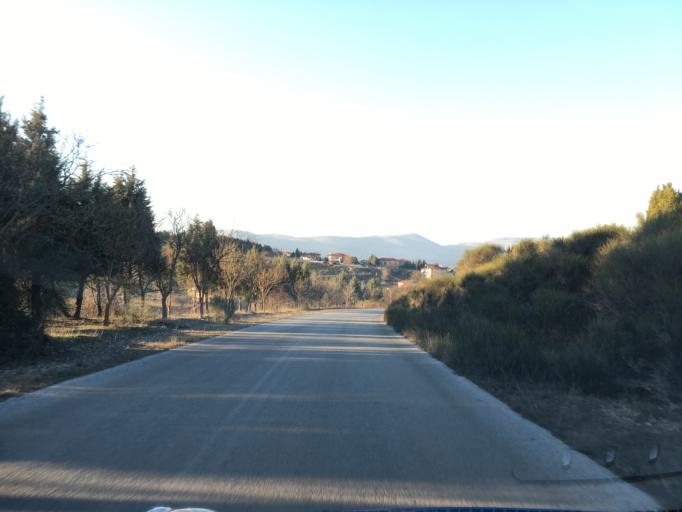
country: GR
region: West Macedonia
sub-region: Nomos Kozanis
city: Kozani
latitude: 40.2815
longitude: 21.7329
